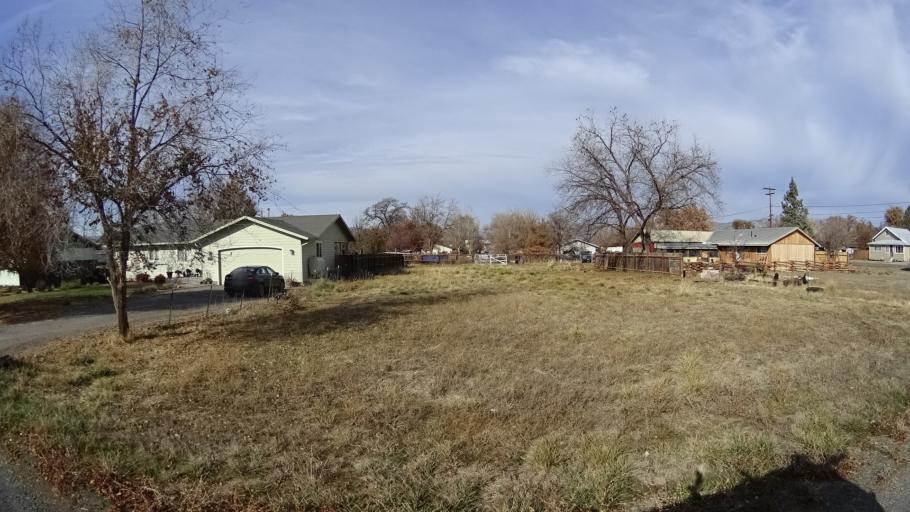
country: US
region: California
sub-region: Siskiyou County
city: Montague
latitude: 41.7249
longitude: -122.5245
